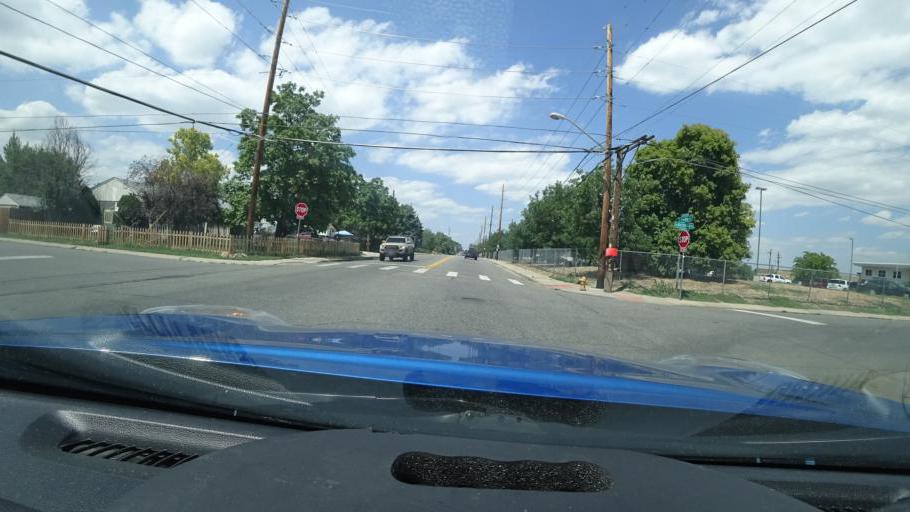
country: US
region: Colorado
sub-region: Arapahoe County
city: Sheridan
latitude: 39.6947
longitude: -105.0297
